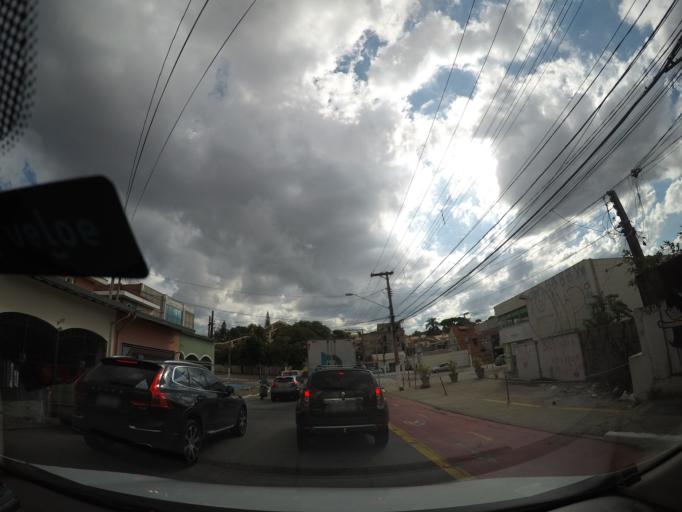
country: BR
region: Sao Paulo
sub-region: Sao Paulo
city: Sao Paulo
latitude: -23.6146
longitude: -46.6433
